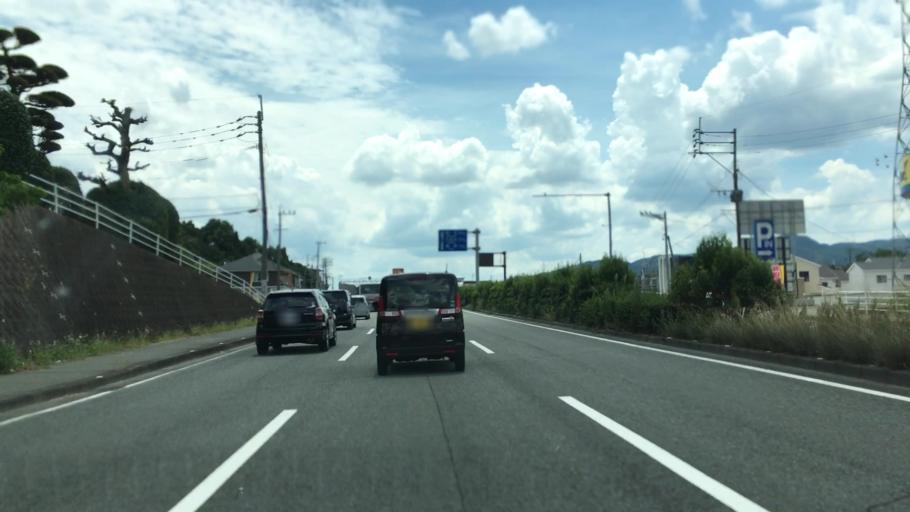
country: JP
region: Fukuoka
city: Chikushino-shi
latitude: 33.4925
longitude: 130.5355
